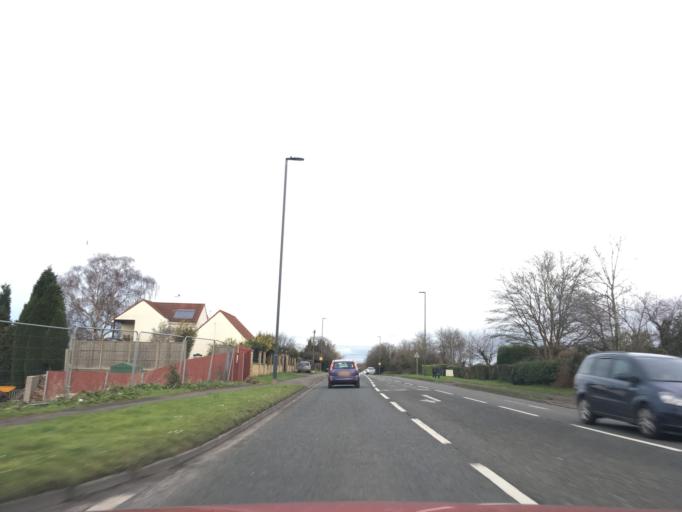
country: GB
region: England
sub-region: South Gloucestershire
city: Almondsbury
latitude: 51.5575
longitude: -2.5632
